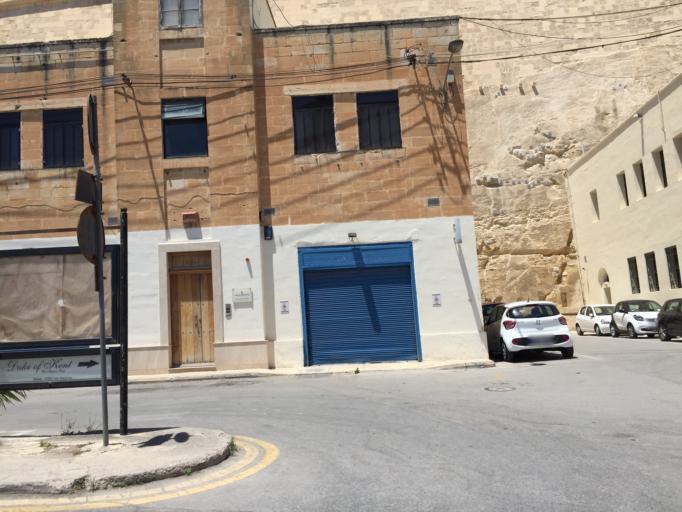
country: MT
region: Il-Furjana
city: Floriana
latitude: 35.8933
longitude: 14.5108
